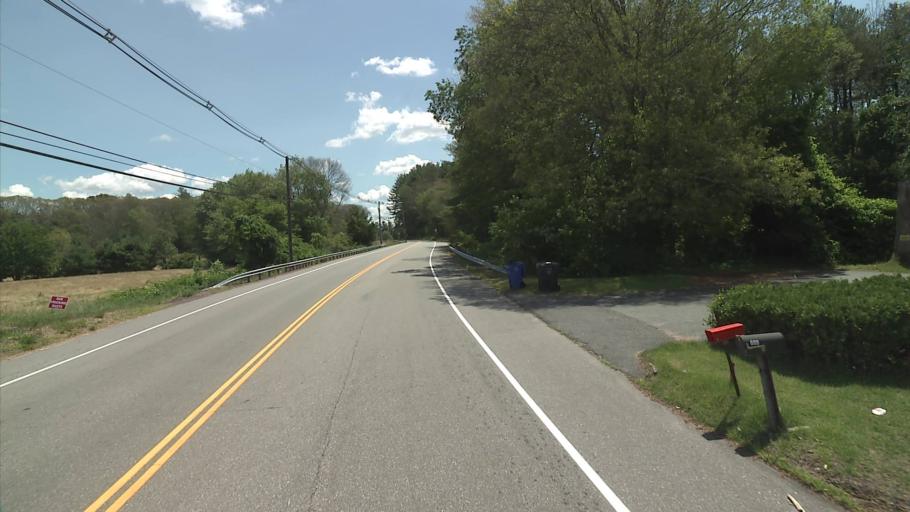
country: US
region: Connecticut
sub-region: New London County
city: Jewett City
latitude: 41.6138
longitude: -71.9440
